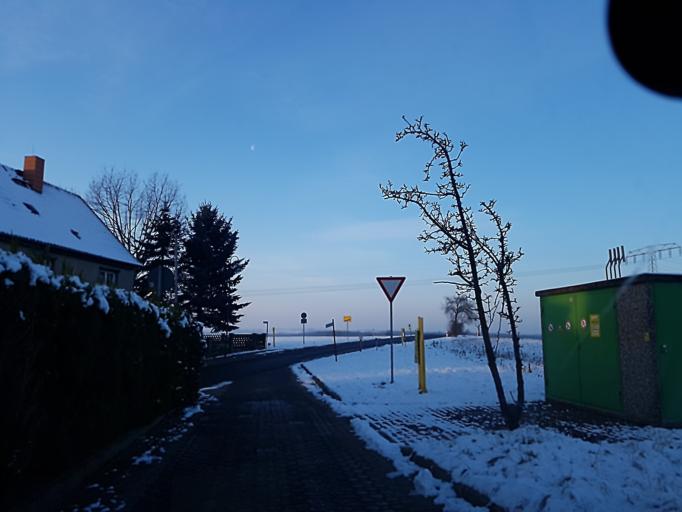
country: DE
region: Saxony
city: Grossweitzschen
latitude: 51.1565
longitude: 13.0404
